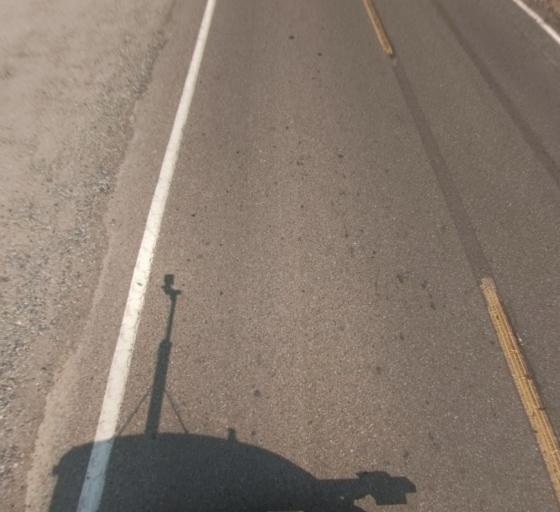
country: US
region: California
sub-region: Madera County
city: Fairmead
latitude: 37.1430
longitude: -120.1619
